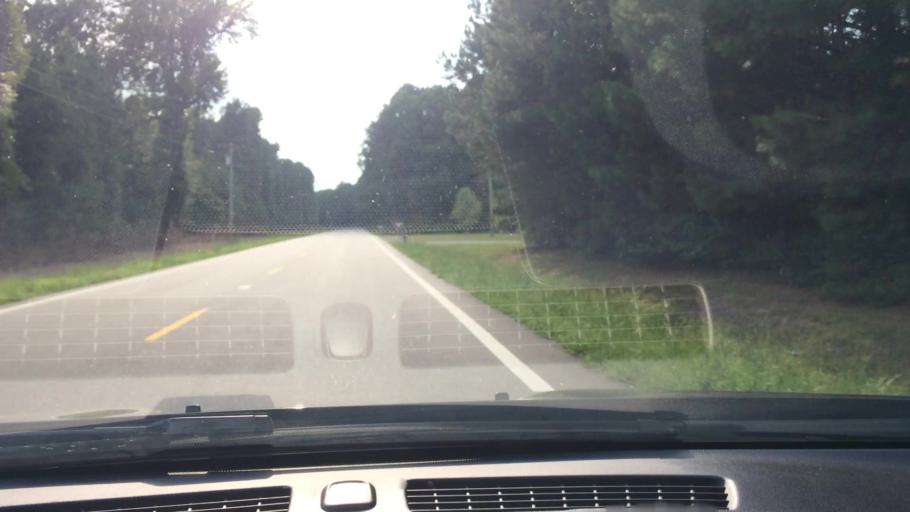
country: US
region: North Carolina
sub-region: Craven County
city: Vanceboro
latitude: 35.4187
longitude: -77.2469
